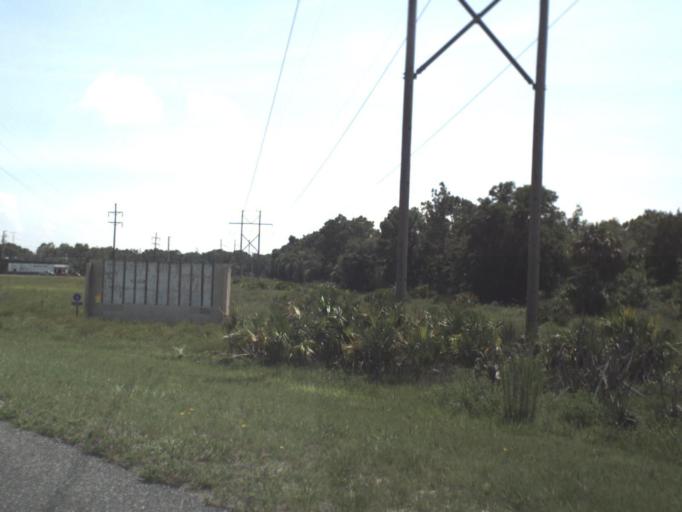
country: US
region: Florida
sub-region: Levy County
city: Inglis
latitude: 29.0375
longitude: -82.6690
